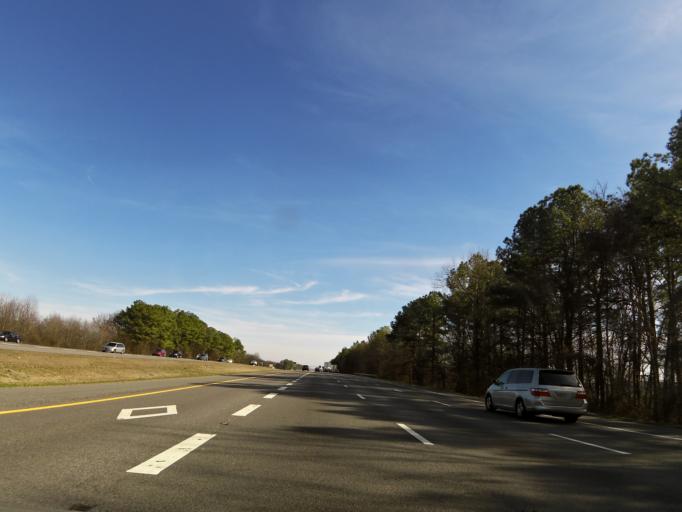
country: US
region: Tennessee
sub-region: Rutherford County
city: Smyrna
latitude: 35.9046
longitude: -86.4986
